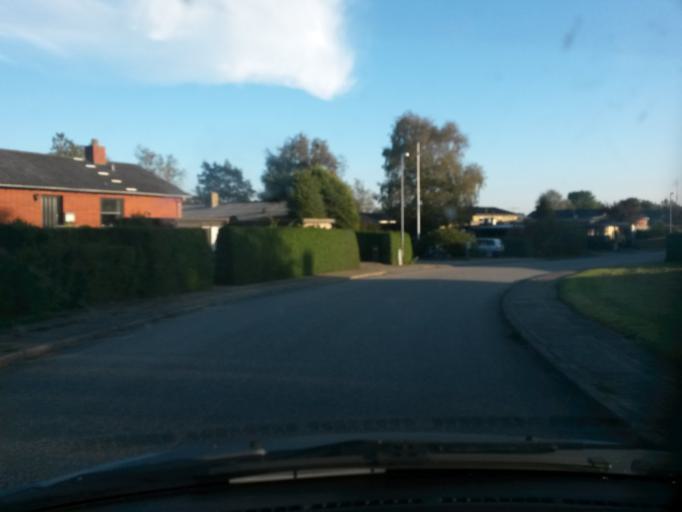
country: DK
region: Central Jutland
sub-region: Silkeborg Kommune
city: Kjellerup
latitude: 56.2757
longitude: 9.3172
